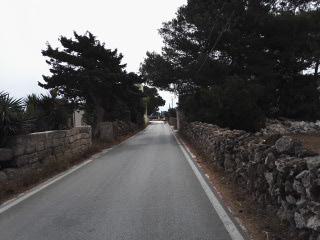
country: IT
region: Sicily
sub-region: Trapani
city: Favignana
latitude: 37.9232
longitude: 12.3378
